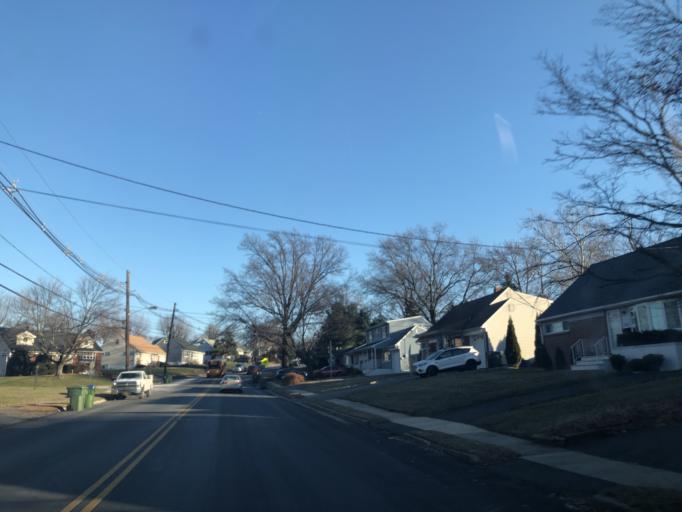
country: US
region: New Jersey
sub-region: Middlesex County
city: Fords
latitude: 40.5396
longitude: -74.3371
